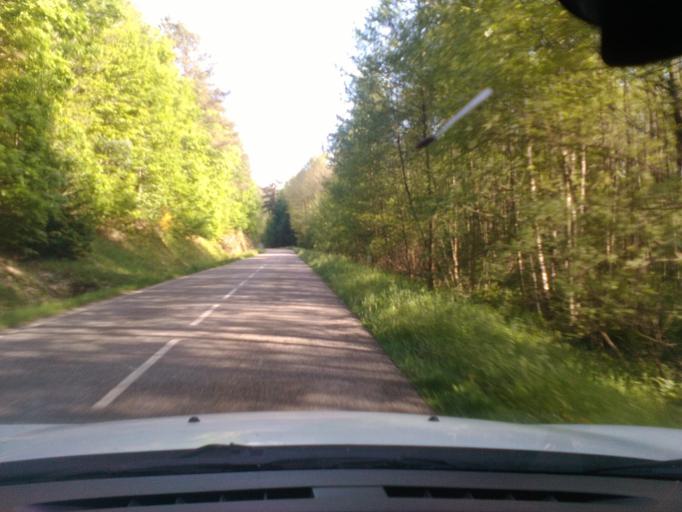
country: FR
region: Lorraine
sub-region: Departement des Vosges
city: Bruyeres
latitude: 48.2700
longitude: 6.7237
